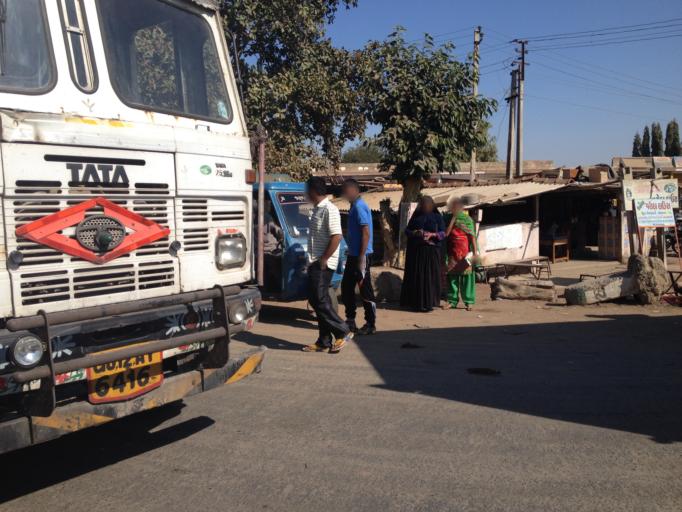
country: IN
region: Gujarat
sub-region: Kachchh
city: Anjar
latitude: 23.1853
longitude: 69.9067
